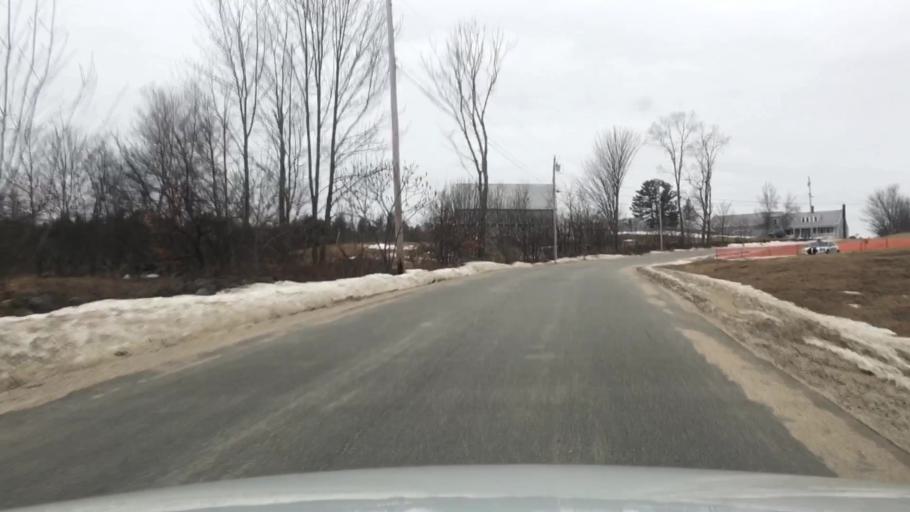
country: US
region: Maine
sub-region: York County
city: Springvale
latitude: 43.4978
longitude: -70.8179
